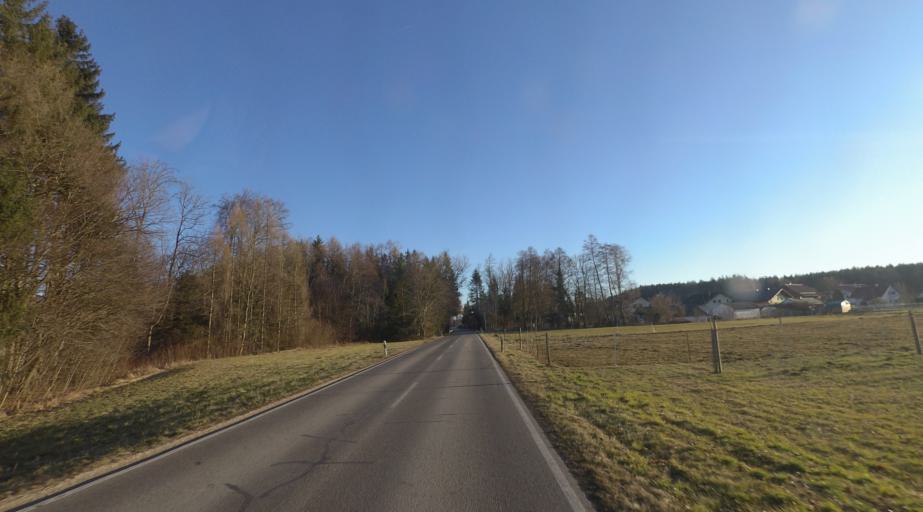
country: DE
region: Bavaria
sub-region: Upper Bavaria
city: Kirchanschoring
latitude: 47.9633
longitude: 12.8246
